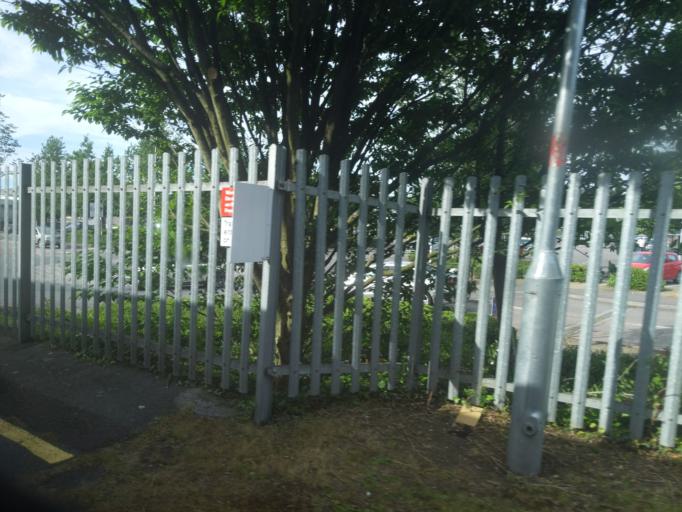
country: GB
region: England
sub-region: Devon
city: Barnstaple
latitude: 51.0731
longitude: -4.0624
